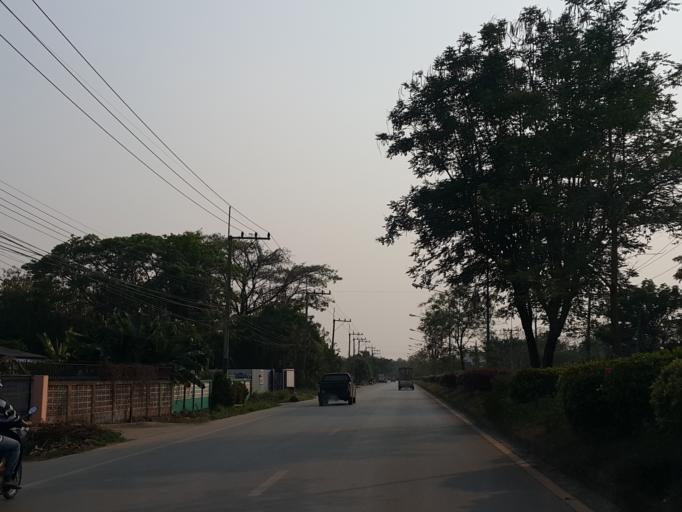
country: TH
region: Lampang
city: Lampang
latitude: 18.3337
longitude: 99.5299
